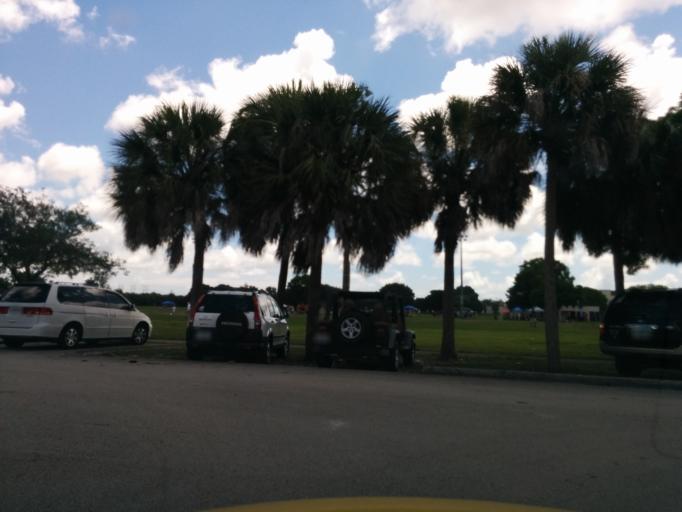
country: US
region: Florida
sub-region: Broward County
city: Cooper City
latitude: 26.0321
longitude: -80.2714
